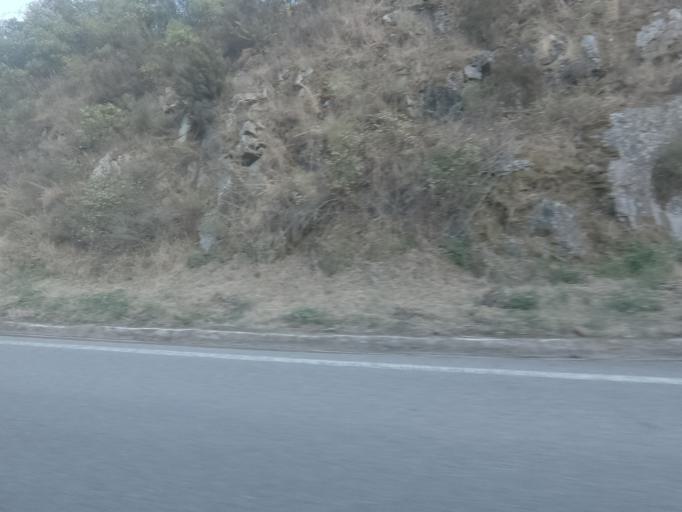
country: PT
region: Viseu
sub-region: Armamar
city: Armamar
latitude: 41.1608
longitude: -7.6656
